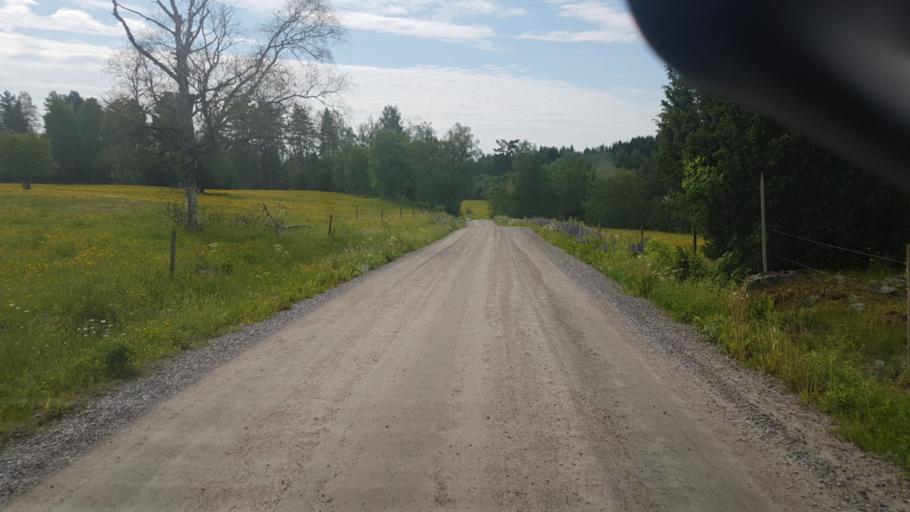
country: SE
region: Vaermland
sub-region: Eda Kommun
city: Amotfors
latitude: 59.7825
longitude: 12.4374
